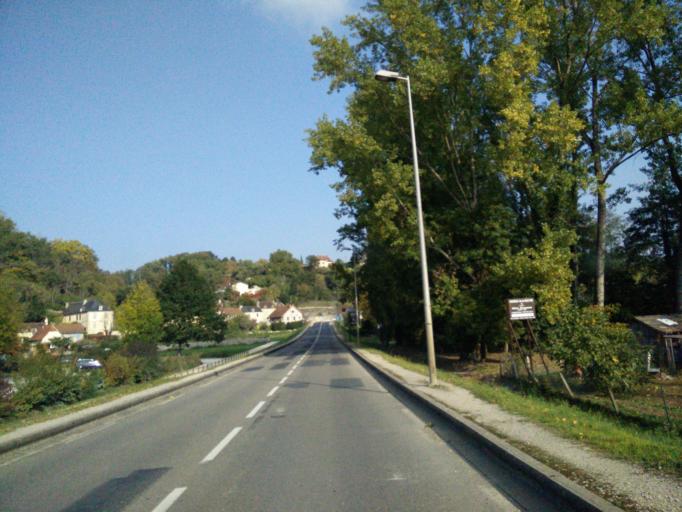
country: FR
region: Aquitaine
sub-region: Departement de la Dordogne
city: Montignac
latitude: 45.0673
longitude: 1.1664
